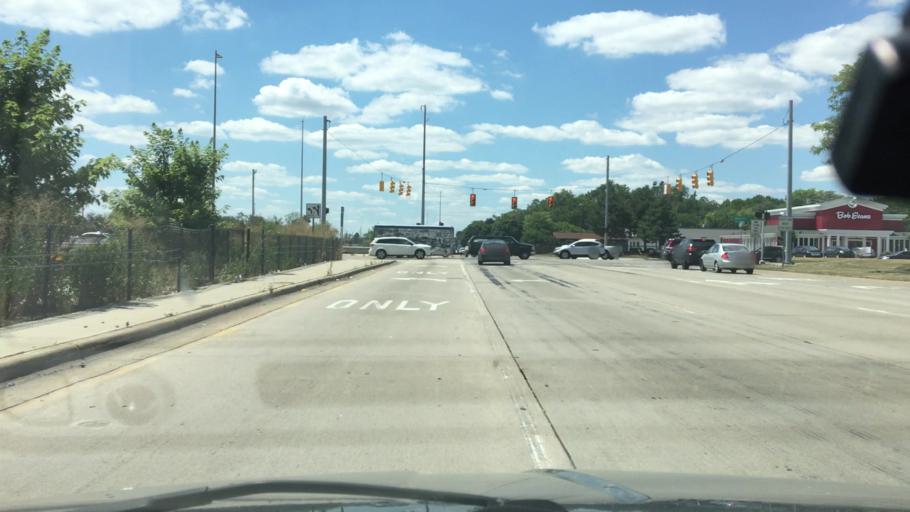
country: US
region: Michigan
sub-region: Wayne County
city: Livonia
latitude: 42.3839
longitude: -83.3328
